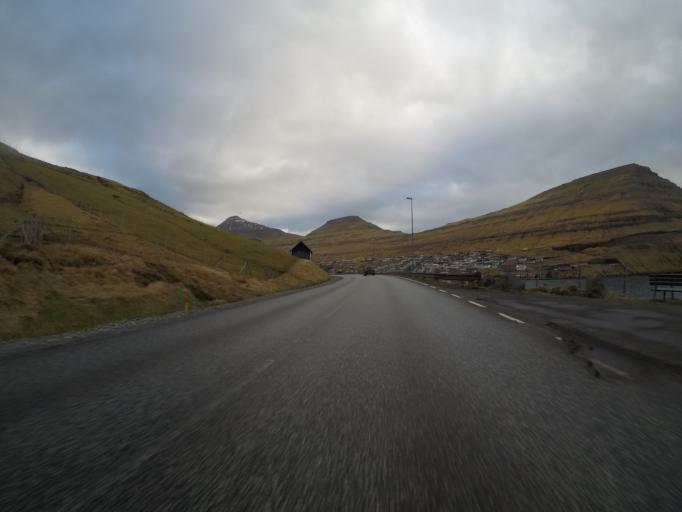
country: FO
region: Nordoyar
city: Klaksvik
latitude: 62.2412
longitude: -6.5919
